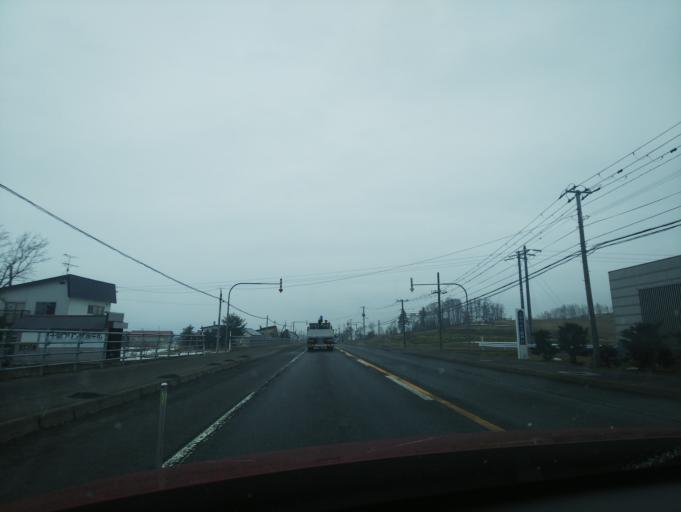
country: JP
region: Hokkaido
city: Nayoro
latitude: 44.1529
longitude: 142.3994
